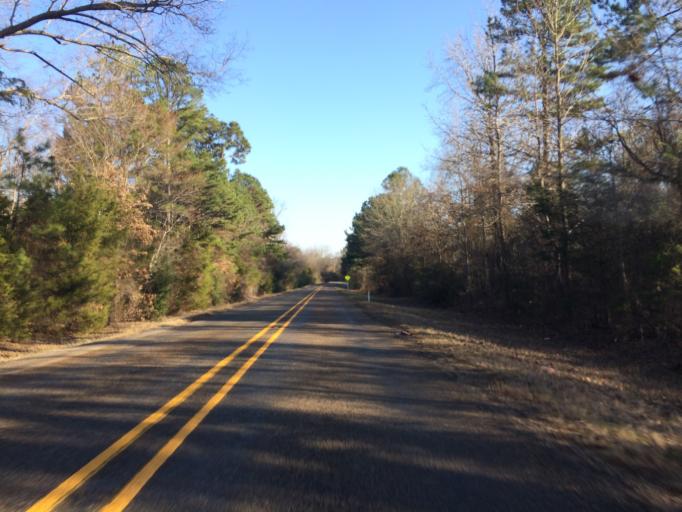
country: US
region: Texas
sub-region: Wood County
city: Hawkins
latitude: 32.6653
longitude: -95.3170
